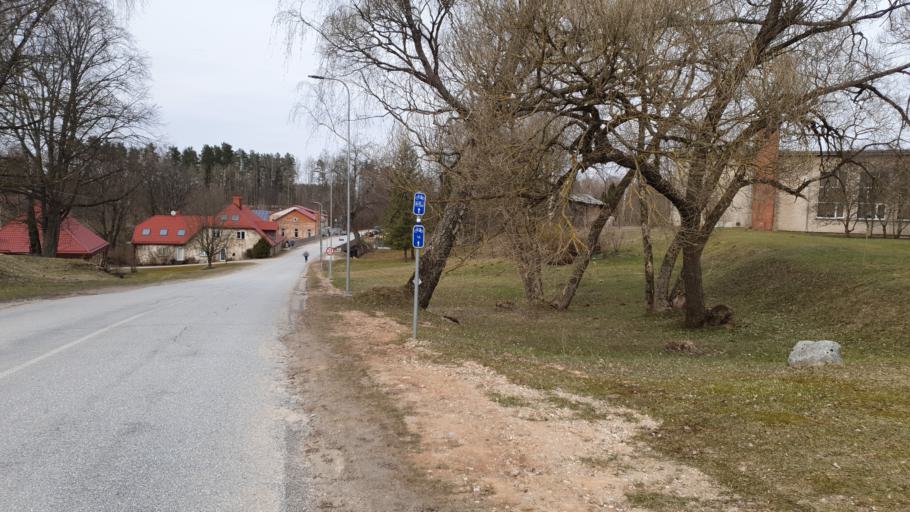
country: LV
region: Beverina
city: Murmuiza
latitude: 57.5467
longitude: 25.5459
